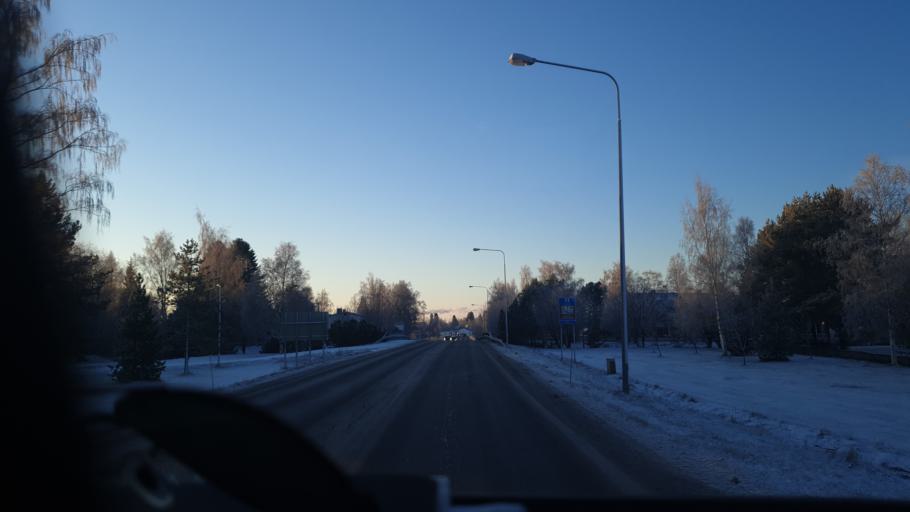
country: FI
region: Northern Ostrobothnia
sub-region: Ylivieska
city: Kalajoki
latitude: 64.2599
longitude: 23.9455
